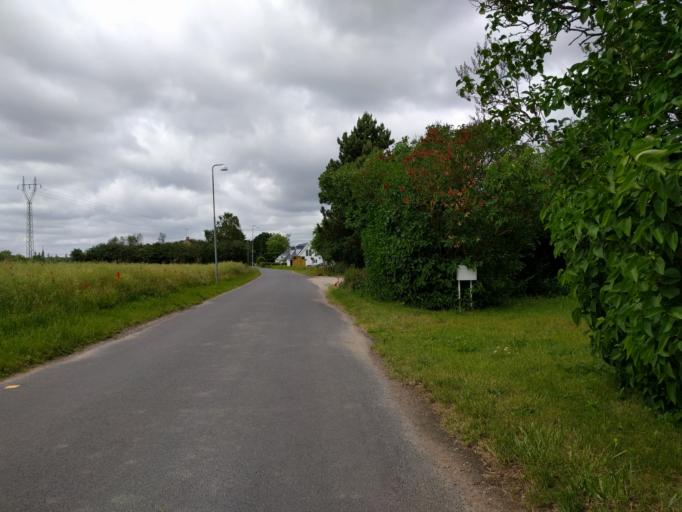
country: DK
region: South Denmark
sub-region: Odense Kommune
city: Bullerup
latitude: 55.4225
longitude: 10.5108
